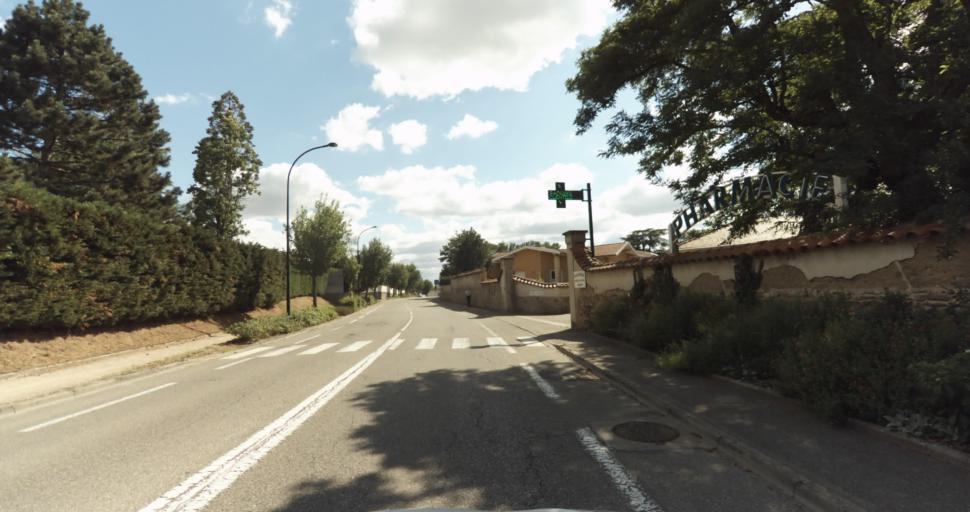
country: FR
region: Rhone-Alpes
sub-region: Departement du Rhone
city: Chaponost
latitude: 45.7169
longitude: 4.7528
